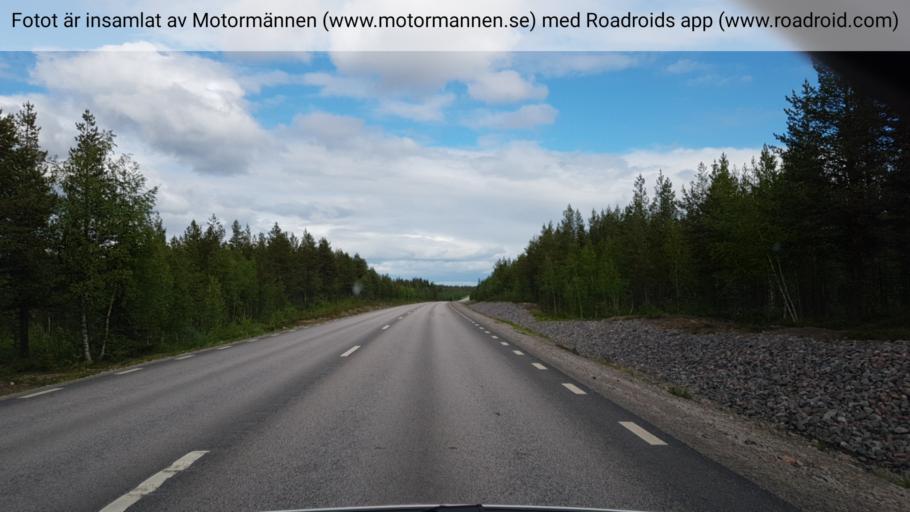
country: SE
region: Norrbotten
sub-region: Gallivare Kommun
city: Malmberget
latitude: 67.6629
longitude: 21.4598
